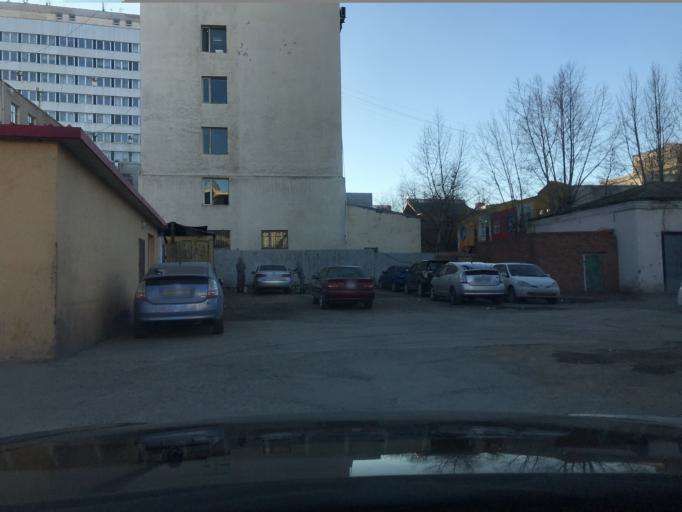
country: MN
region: Ulaanbaatar
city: Ulaanbaatar
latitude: 47.9229
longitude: 106.9086
